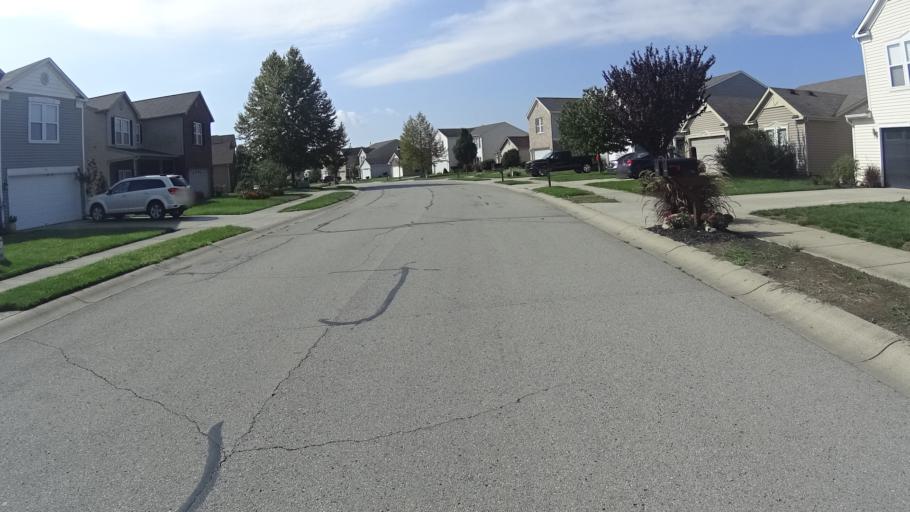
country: US
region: Indiana
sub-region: Hancock County
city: Fortville
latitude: 39.9840
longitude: -85.8557
